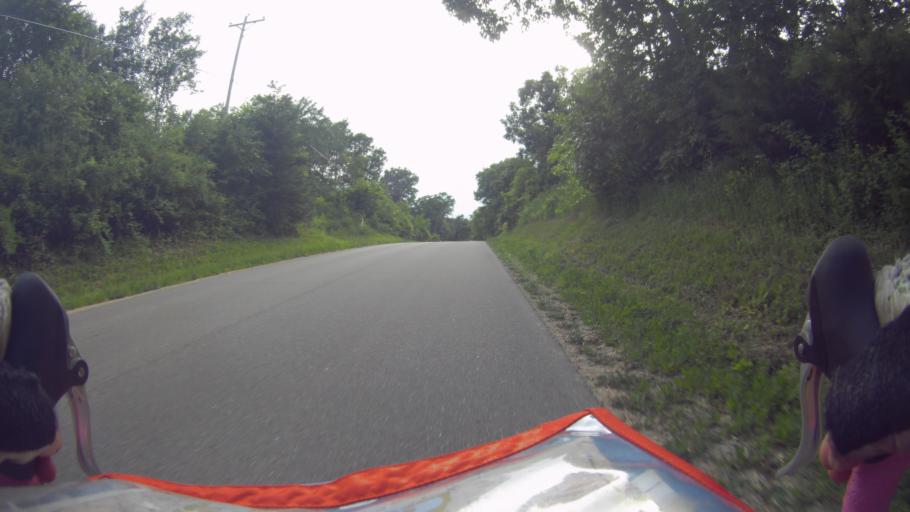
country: US
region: Wisconsin
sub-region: Dane County
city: Monona
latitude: 43.0042
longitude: -89.3589
